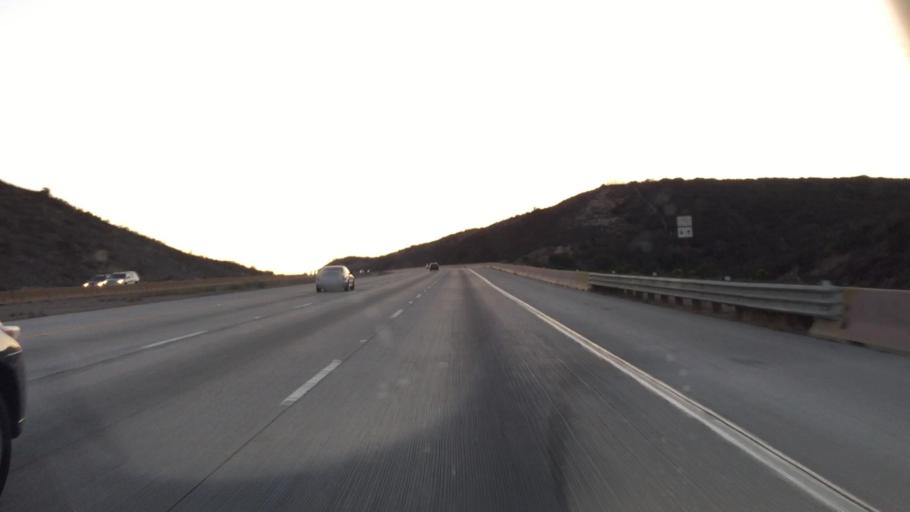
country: US
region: California
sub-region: San Diego County
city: Santee
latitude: 32.8545
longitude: -117.0581
